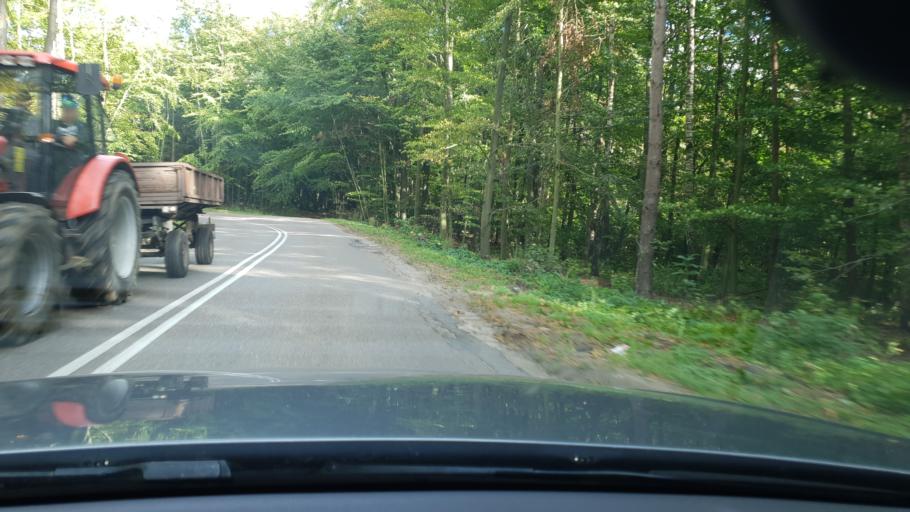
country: PL
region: Pomeranian Voivodeship
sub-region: Powiat wejherowski
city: Bojano
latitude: 54.5092
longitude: 18.3841
